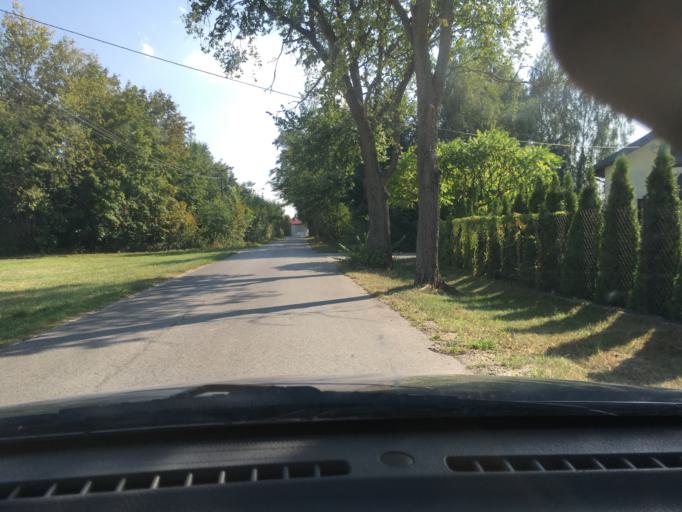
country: PL
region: Masovian Voivodeship
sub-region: Powiat piaseczynski
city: Lesznowola
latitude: 52.0501
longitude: 20.9447
